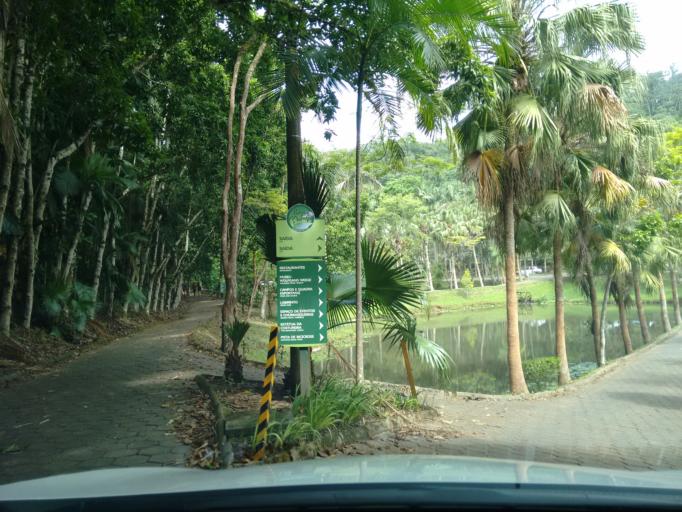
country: BR
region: Santa Catarina
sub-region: Jaragua Do Sul
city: Jaragua do Sul
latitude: -26.5057
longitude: -49.1258
